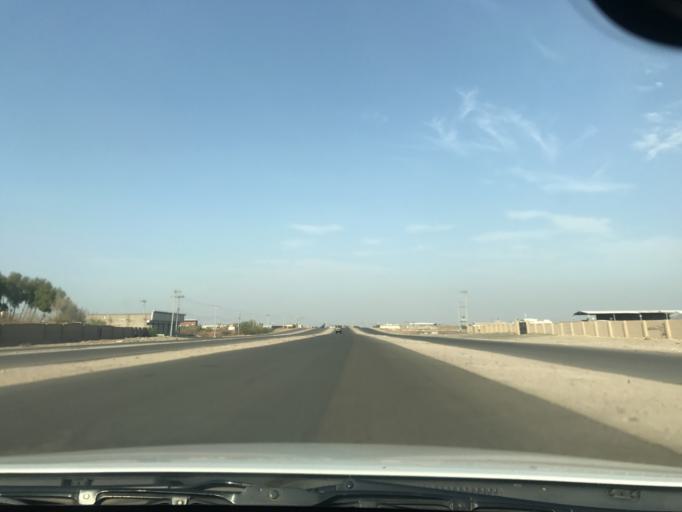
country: SA
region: Makkah
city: Al Jumum
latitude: 21.4522
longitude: 39.5288
